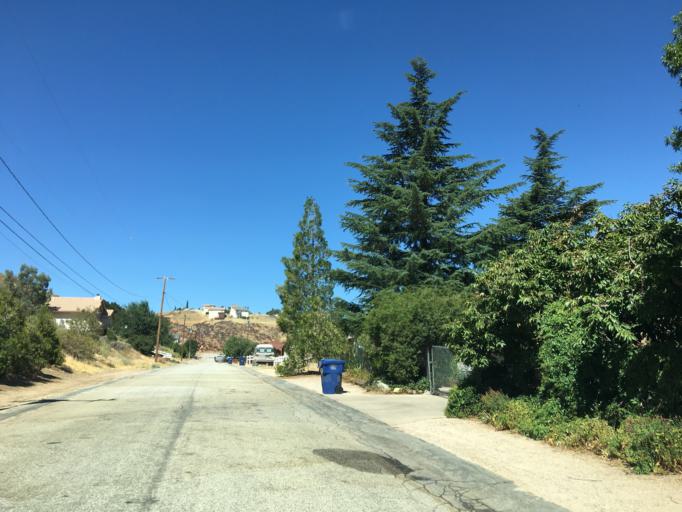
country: US
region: California
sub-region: Los Angeles County
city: Green Valley
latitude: 34.6570
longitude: -118.3784
